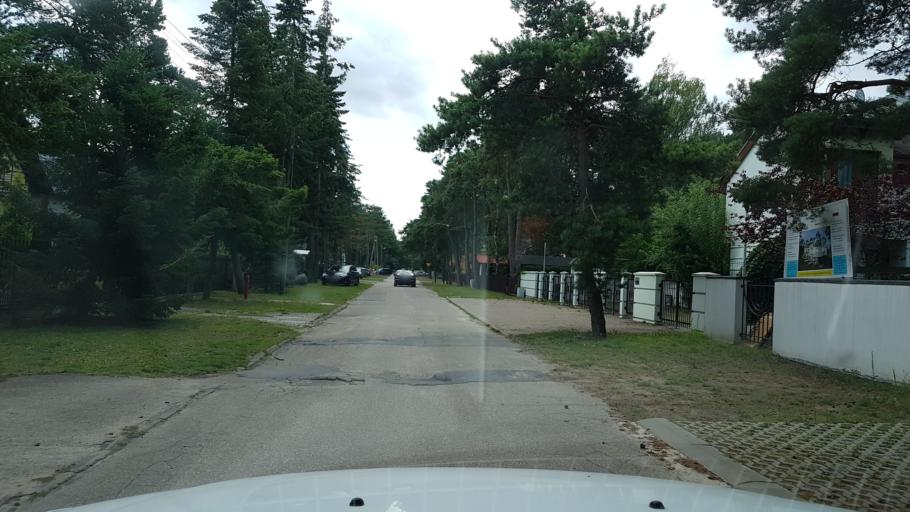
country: PL
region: West Pomeranian Voivodeship
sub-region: Powiat gryficki
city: Pobierowo
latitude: 54.0610
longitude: 14.9433
